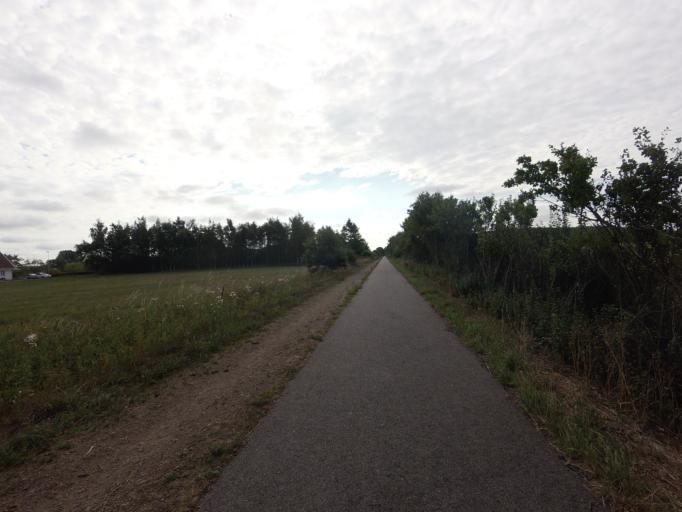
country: SE
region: Skane
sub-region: Helsingborg
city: Odakra
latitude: 56.1748
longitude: 12.6897
